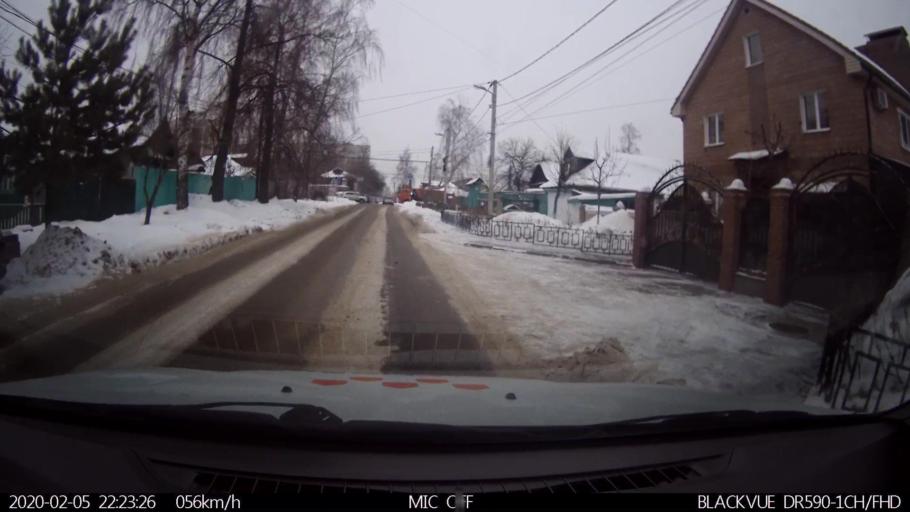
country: RU
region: Nizjnij Novgorod
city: Pervomaysk
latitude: 54.7661
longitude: 44.0282
